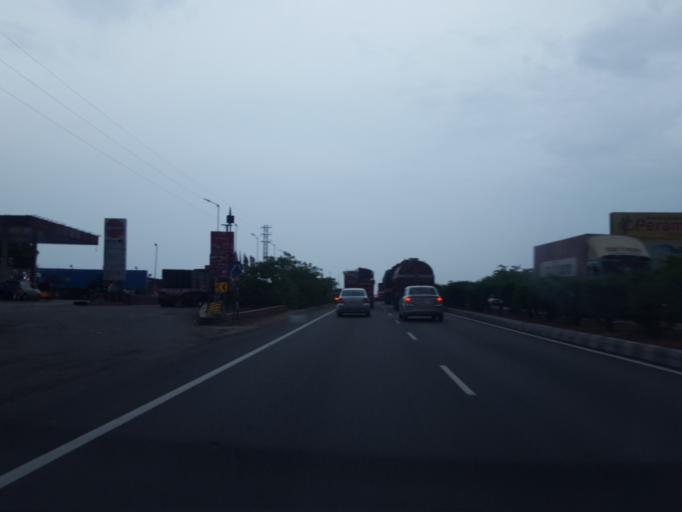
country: IN
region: Telangana
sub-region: Mahbubnagar
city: Farrukhnagar
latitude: 17.1039
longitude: 78.2549
